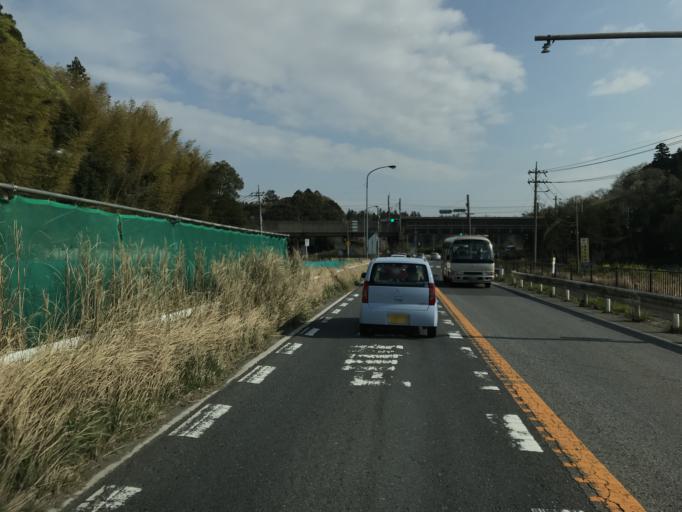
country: JP
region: Chiba
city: Narita
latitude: 35.7939
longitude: 140.3377
